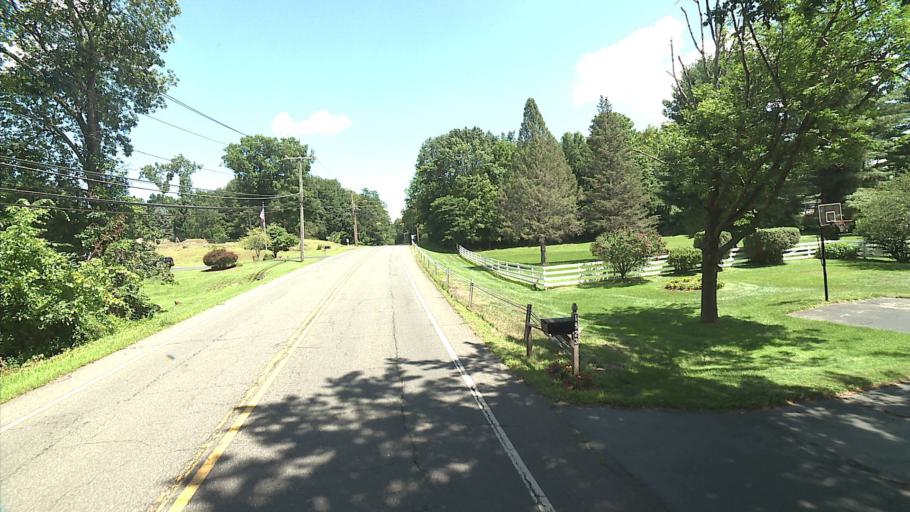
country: US
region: Connecticut
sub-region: Hartford County
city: Suffield Depot
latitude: 41.9931
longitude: -72.7164
